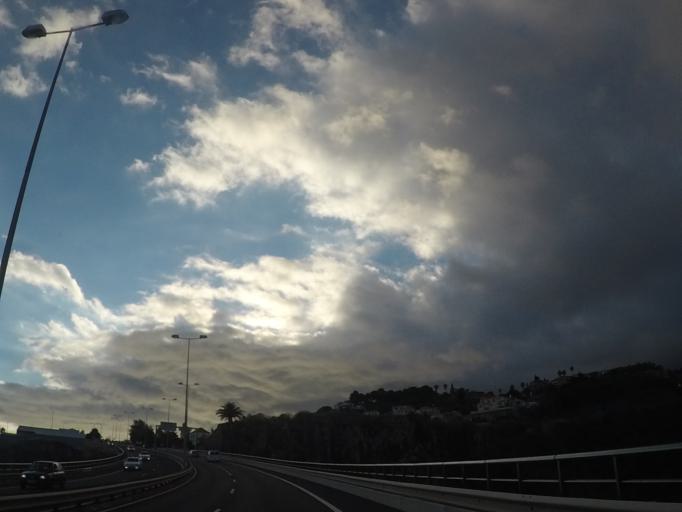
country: PT
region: Madeira
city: Canico
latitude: 32.6495
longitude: -16.8311
